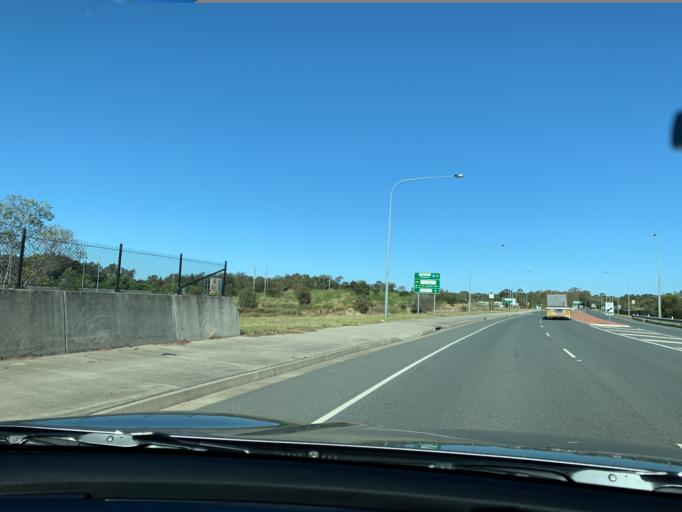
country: AU
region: Queensland
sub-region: Brisbane
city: Wynnum
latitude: -27.4250
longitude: 153.1500
